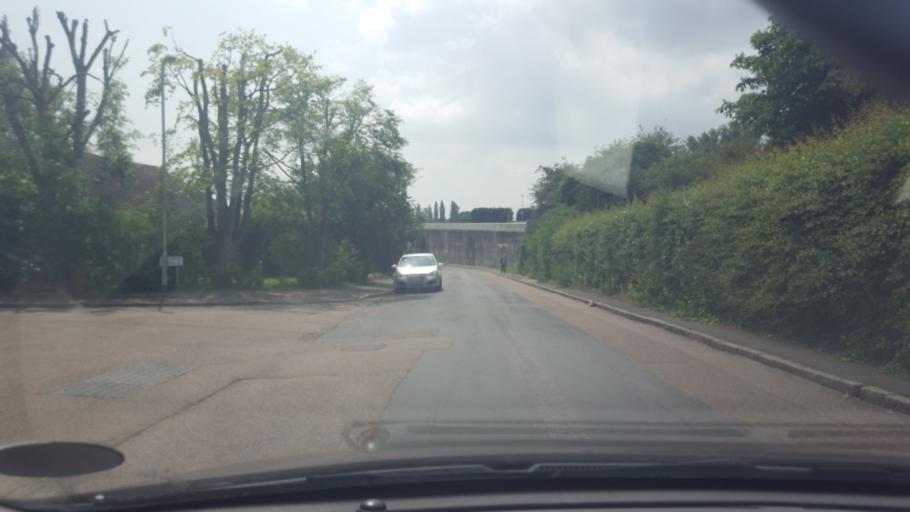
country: GB
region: England
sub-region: Essex
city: Little Clacton
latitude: 51.8548
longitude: 1.1160
